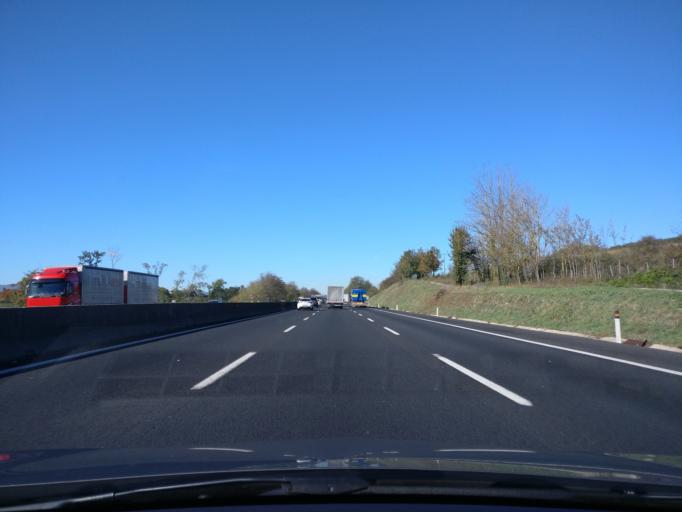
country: IT
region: Latium
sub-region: Citta metropolitana di Roma Capitale
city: Valmontone
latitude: 41.7593
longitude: 12.9561
